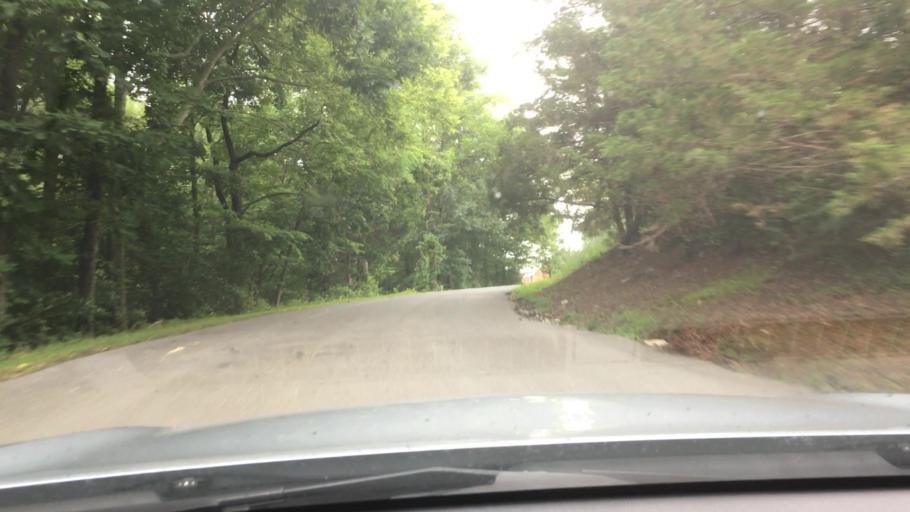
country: US
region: Pennsylvania
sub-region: Franklin County
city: Greencastle
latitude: 39.8747
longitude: -77.7866
